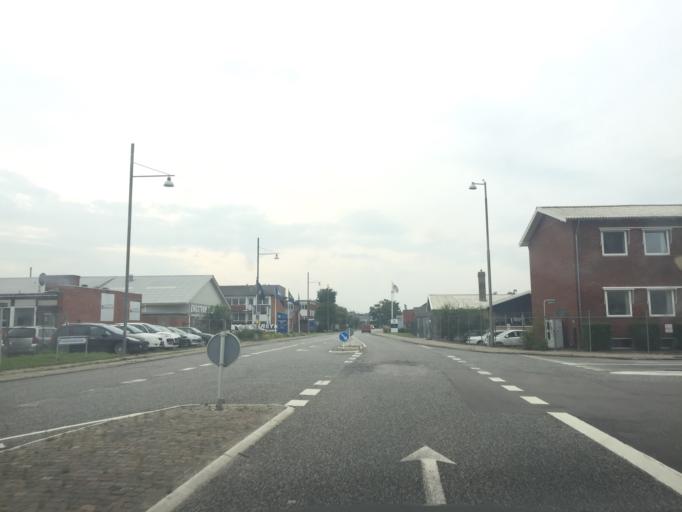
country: DK
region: Capital Region
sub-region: Albertslund Kommune
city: Albertslund
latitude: 55.6614
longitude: 12.3743
